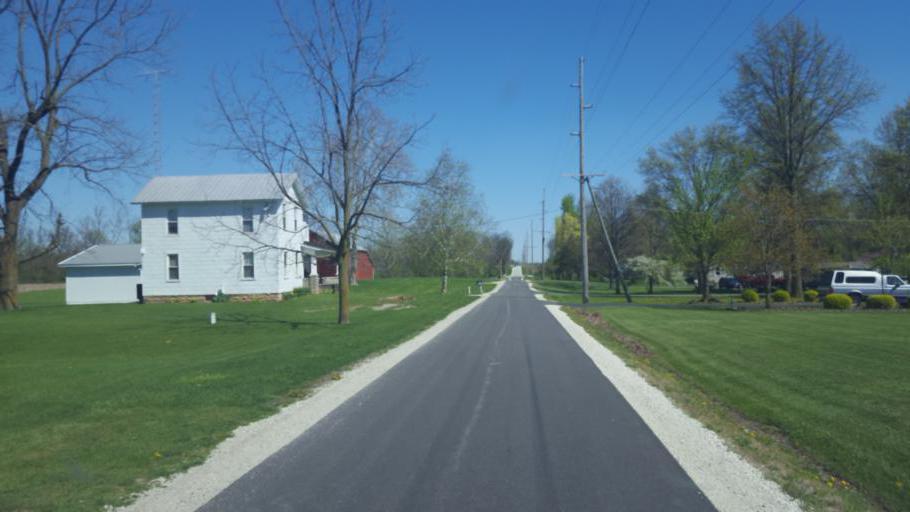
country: US
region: Ohio
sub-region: Sandusky County
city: Ballville
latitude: 41.2676
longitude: -83.1879
